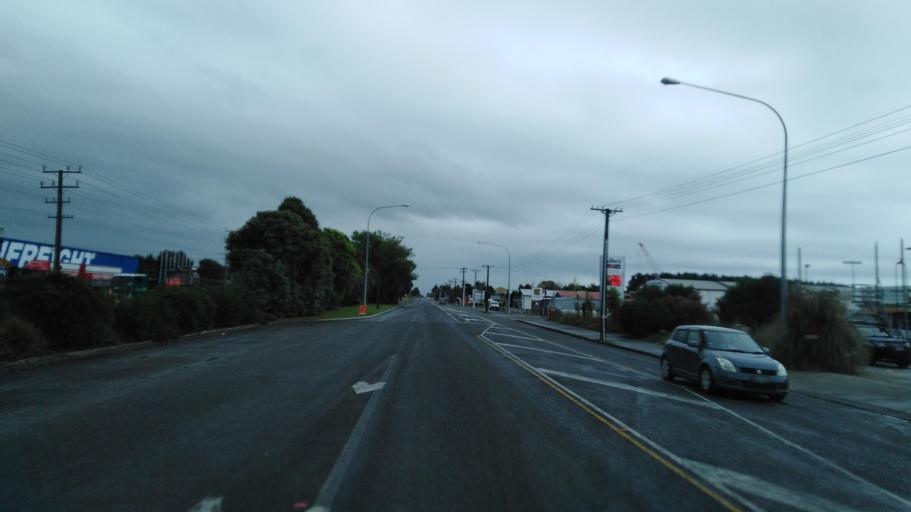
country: NZ
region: Manawatu-Wanganui
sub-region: Horowhenua District
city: Levin
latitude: -40.6363
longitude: 175.2726
